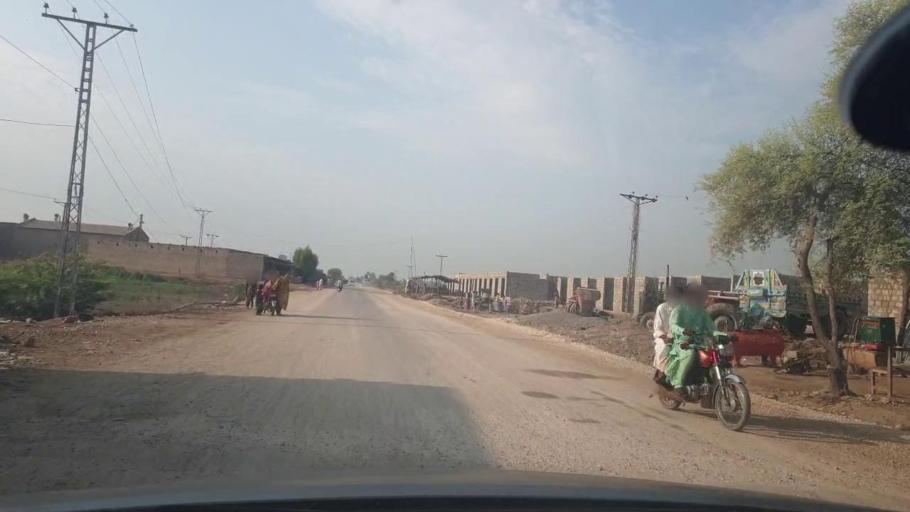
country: PK
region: Sindh
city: Jacobabad
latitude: 28.2140
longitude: 68.3686
